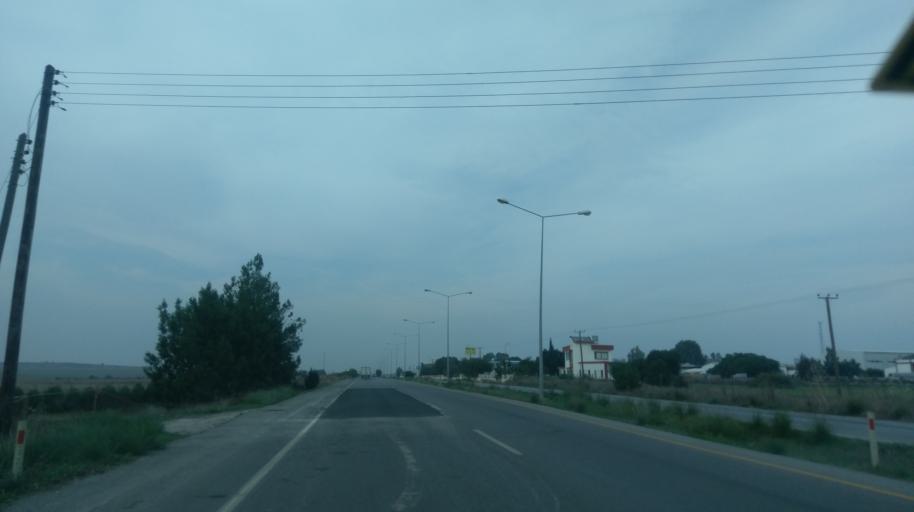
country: CY
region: Lefkosia
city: Mammari
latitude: 35.2124
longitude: 33.2593
